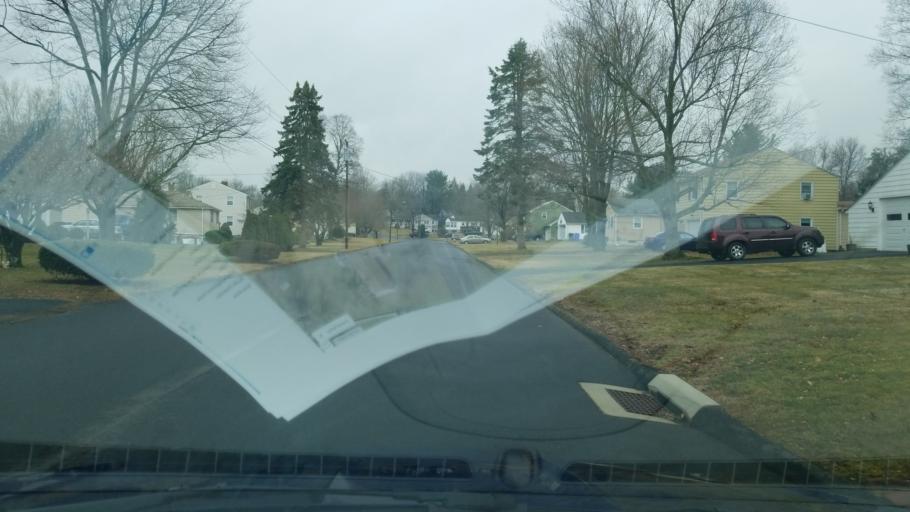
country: US
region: Connecticut
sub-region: Hartford County
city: Wethersfield
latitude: 41.6729
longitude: -72.6709
